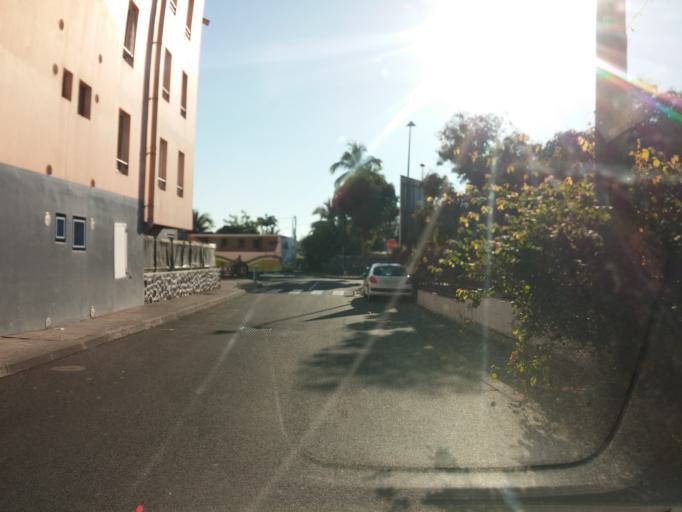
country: RE
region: Reunion
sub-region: Reunion
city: Le Port
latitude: -20.9347
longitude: 55.2955
